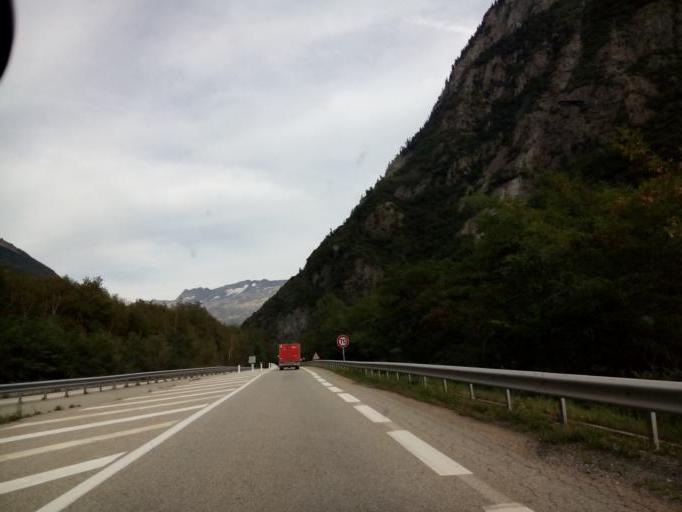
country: FR
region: Rhone-Alpes
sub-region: Departement de l'Isere
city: Livet-et-Gavet
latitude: 45.1134
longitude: 5.9527
